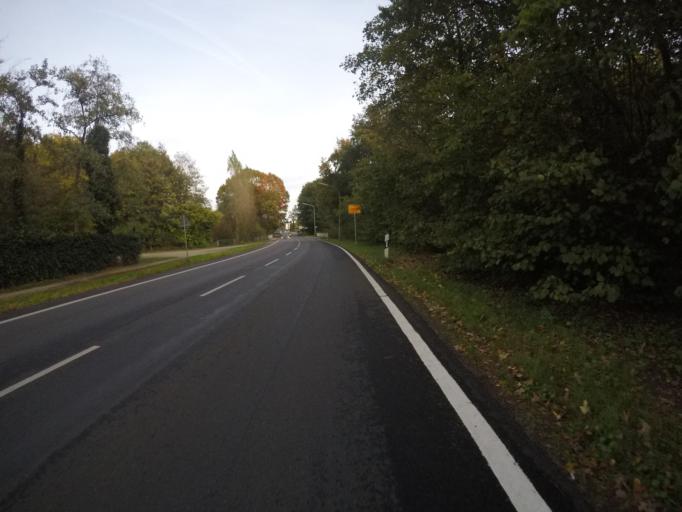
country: DE
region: North Rhine-Westphalia
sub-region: Regierungsbezirk Munster
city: Rhede
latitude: 51.8292
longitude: 6.6880
